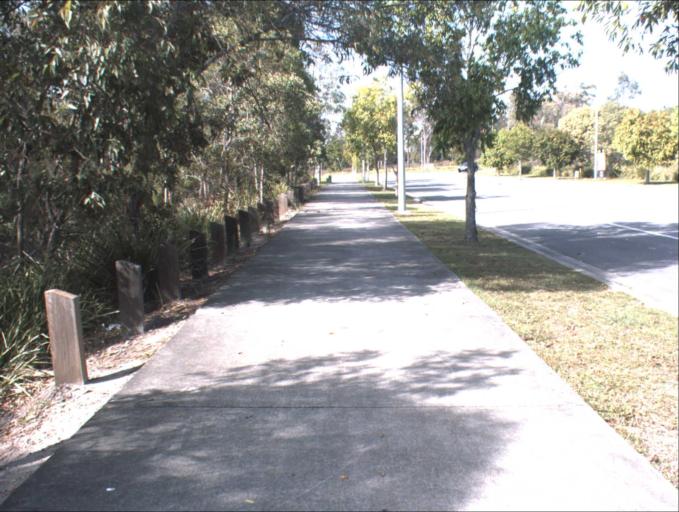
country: AU
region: Queensland
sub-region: Logan
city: Woodridge
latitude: -27.6735
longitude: 153.0794
